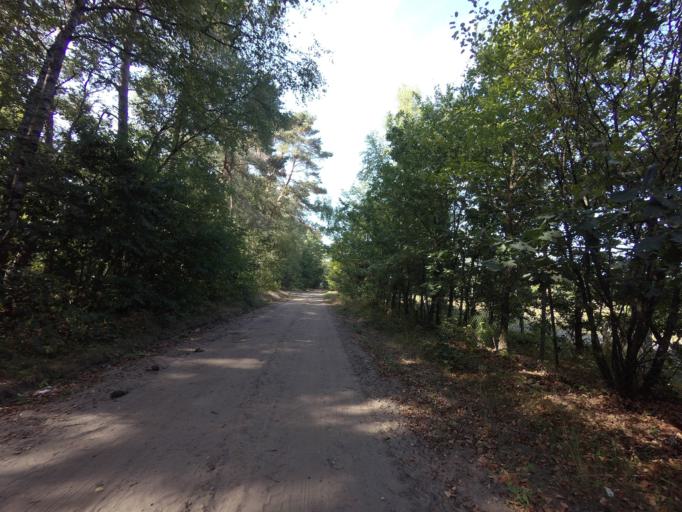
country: NL
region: Gelderland
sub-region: Gemeente Apeldoorn
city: Loenen
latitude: 52.1414
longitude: 6.0246
